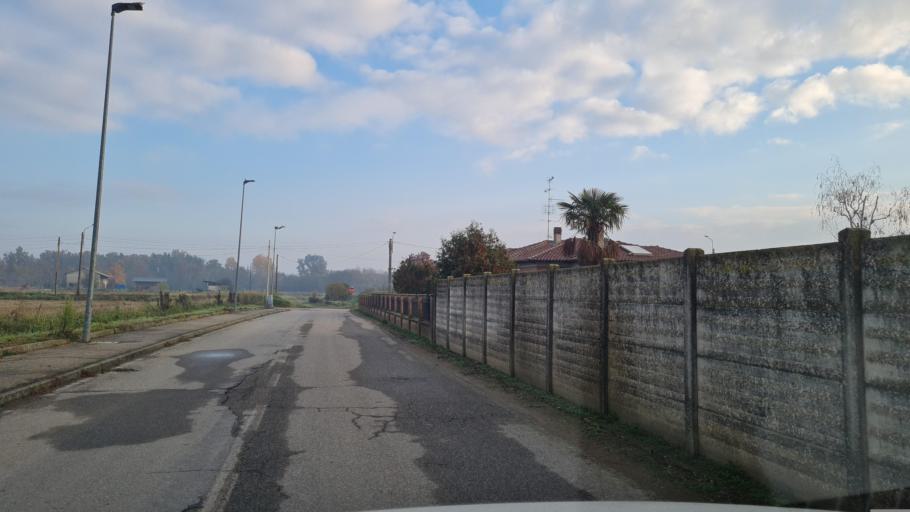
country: IT
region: Piedmont
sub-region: Provincia di Vercelli
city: Villarboit
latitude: 45.4393
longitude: 8.3345
